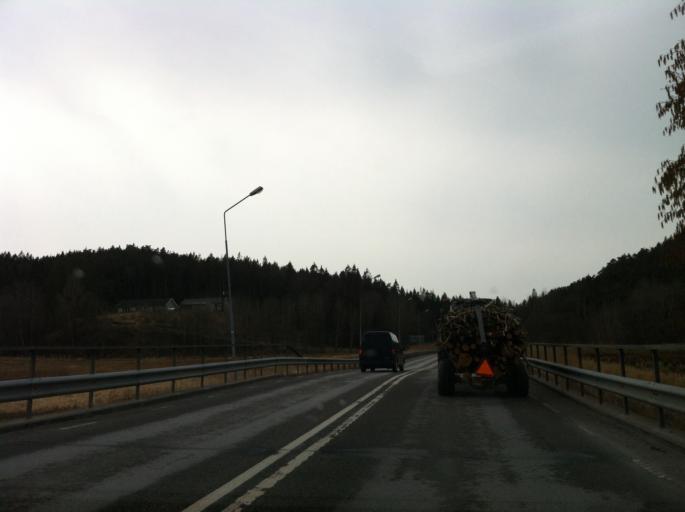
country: SE
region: Vaestra Goetaland
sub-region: Orust
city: Henan
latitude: 58.3145
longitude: 11.6888
